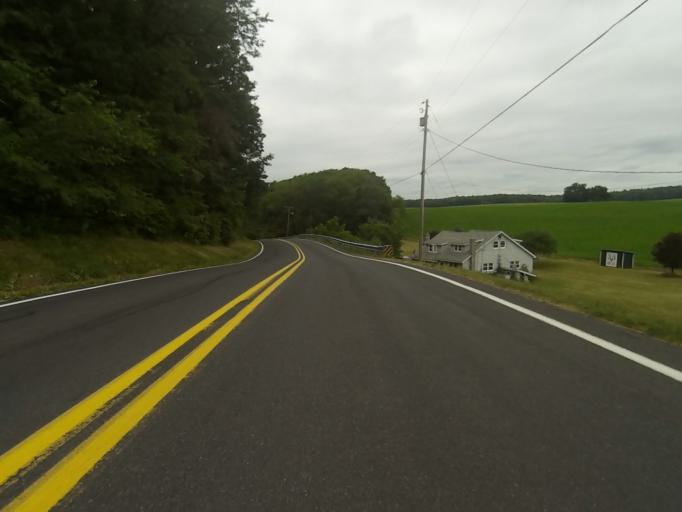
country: US
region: Pennsylvania
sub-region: Centre County
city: Stormstown
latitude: 40.7312
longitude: -78.0360
